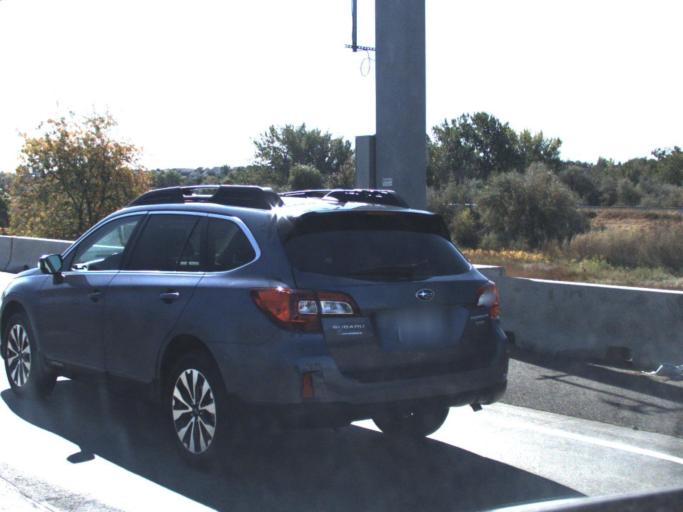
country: US
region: Washington
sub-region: Benton County
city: Richland
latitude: 46.2461
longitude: -119.2509
